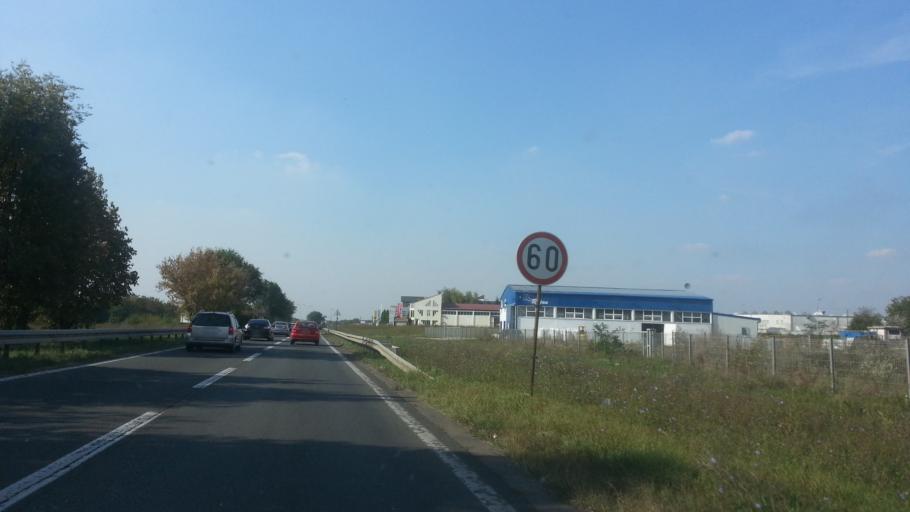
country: RS
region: Central Serbia
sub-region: Belgrade
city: Zemun
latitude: 44.8696
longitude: 20.3384
